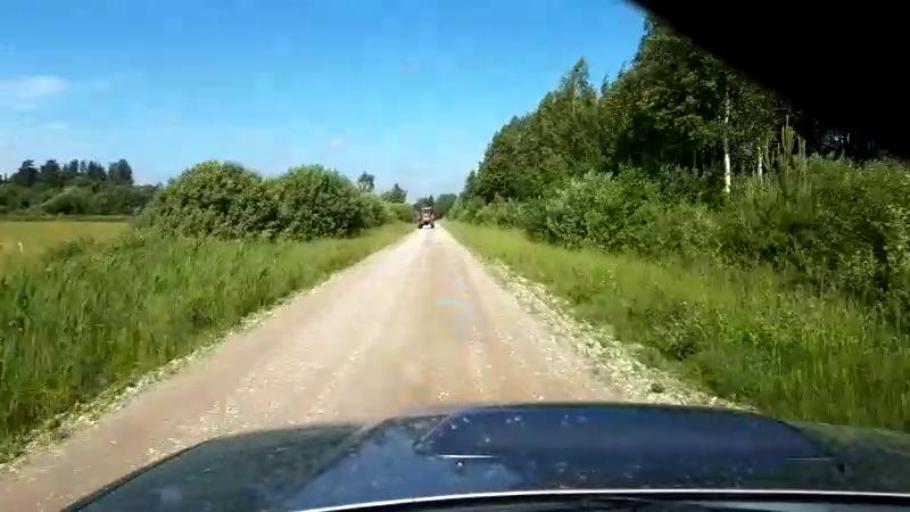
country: EE
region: Paernumaa
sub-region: Sindi linn
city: Sindi
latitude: 58.5128
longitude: 24.6678
